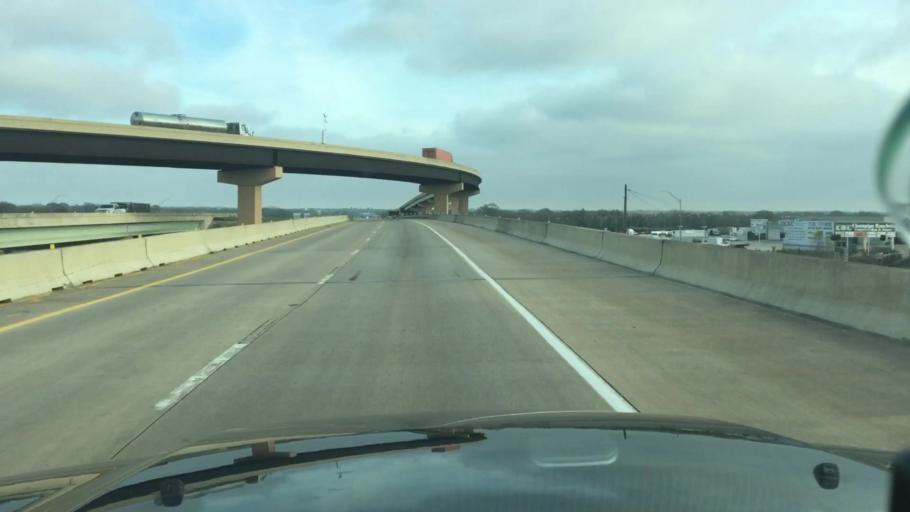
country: US
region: Texas
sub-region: Waller County
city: Hempstead
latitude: 30.1148
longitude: -96.0729
